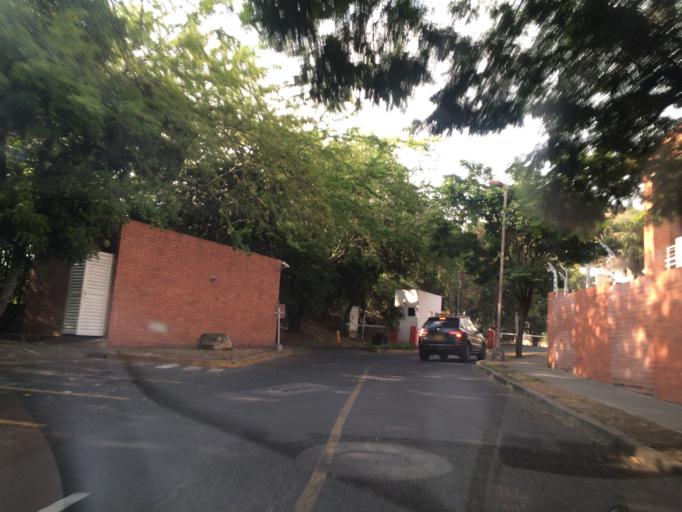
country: CO
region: Valle del Cauca
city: Cali
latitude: 3.4587
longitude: -76.5517
